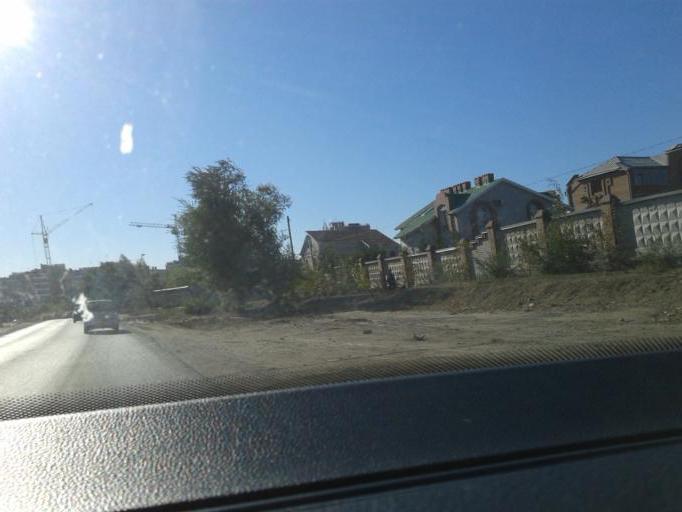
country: RU
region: Volgograd
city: Gorodishche
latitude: 48.7689
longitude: 44.5078
